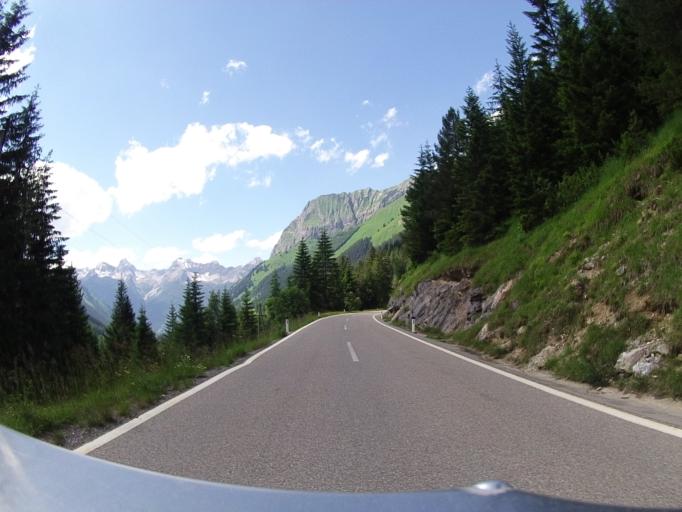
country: AT
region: Tyrol
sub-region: Politischer Bezirk Reutte
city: Elmen
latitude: 47.3017
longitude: 10.5980
